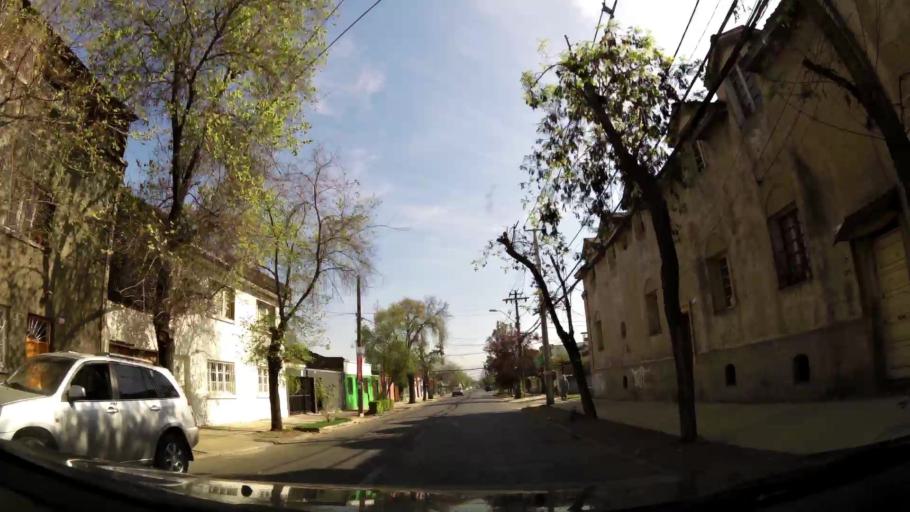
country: CL
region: Santiago Metropolitan
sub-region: Provincia de Santiago
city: Santiago
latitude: -33.4089
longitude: -70.6566
